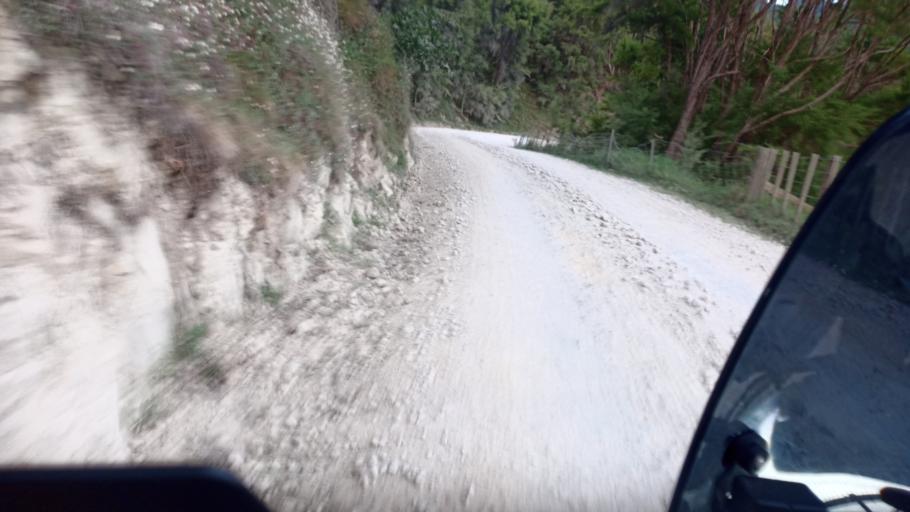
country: NZ
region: Gisborne
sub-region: Gisborne District
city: Gisborne
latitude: -38.4755
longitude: 177.9747
